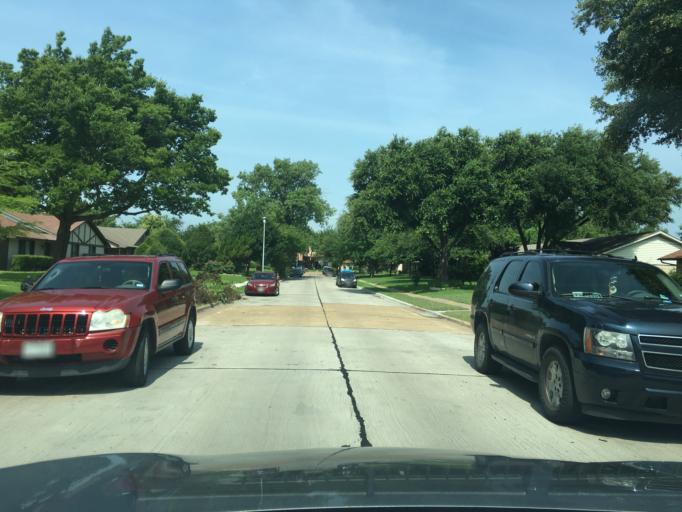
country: US
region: Texas
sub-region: Dallas County
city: Garland
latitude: 32.9250
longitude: -96.6745
